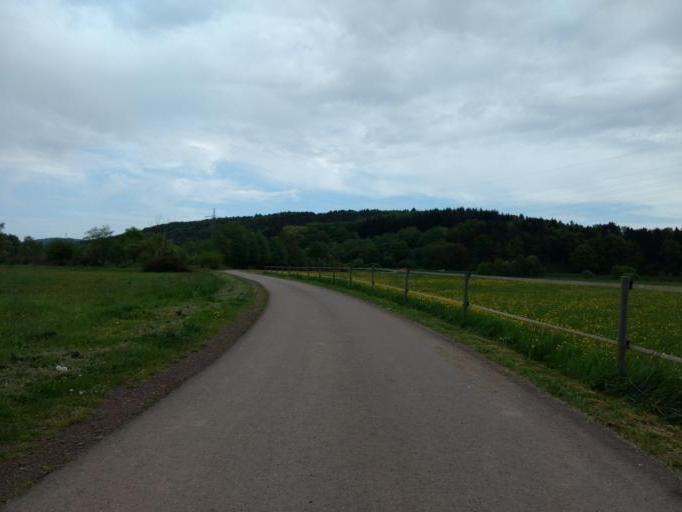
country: DE
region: Saarland
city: Nalbach
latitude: 49.3760
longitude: 6.7955
